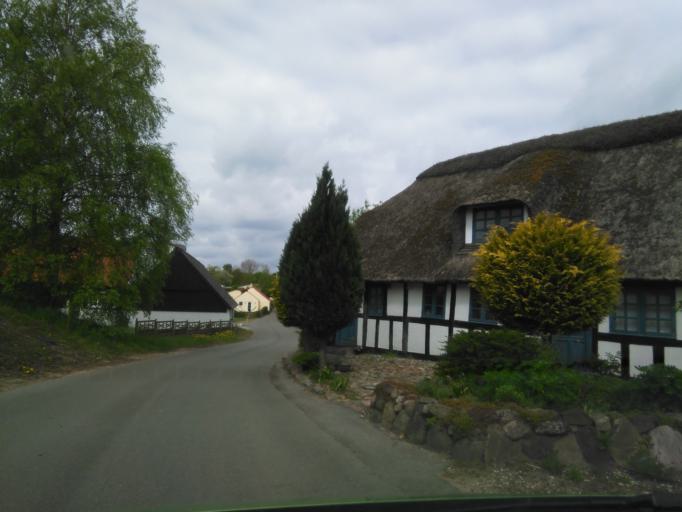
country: DK
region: Central Jutland
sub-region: Skanderborg Kommune
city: Ry
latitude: 56.0688
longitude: 9.8394
